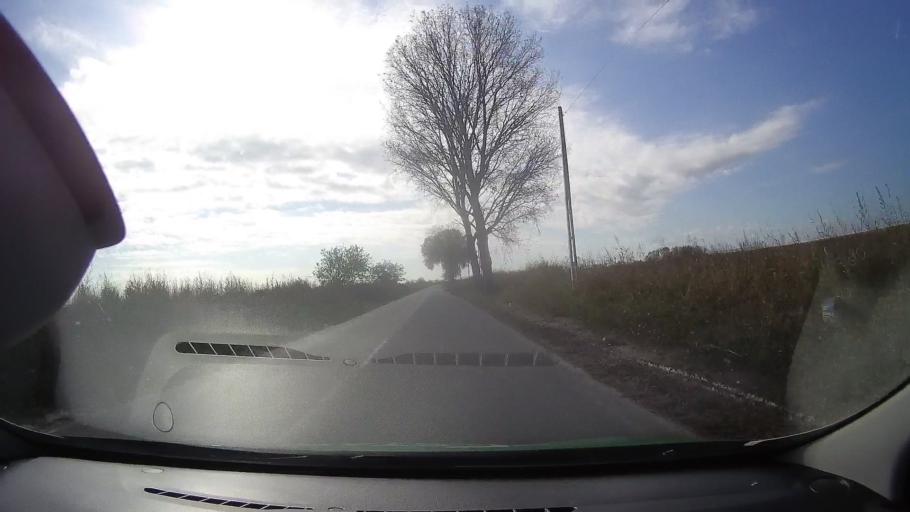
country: RO
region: Tulcea
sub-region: Comuna Valea Nucarilor
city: Agighiol
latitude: 44.9862
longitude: 28.8844
